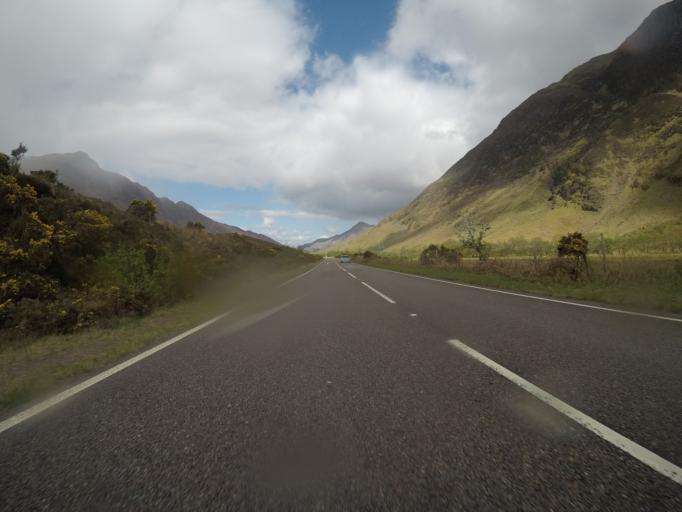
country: GB
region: Scotland
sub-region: Highland
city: Fort William
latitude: 57.1733
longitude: -5.3613
